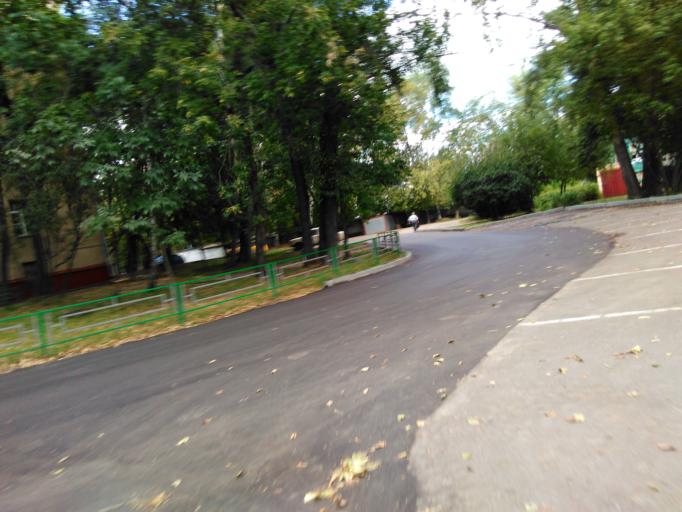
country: RU
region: Moscow
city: Novyye Cheremushki
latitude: 55.6920
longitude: 37.6142
